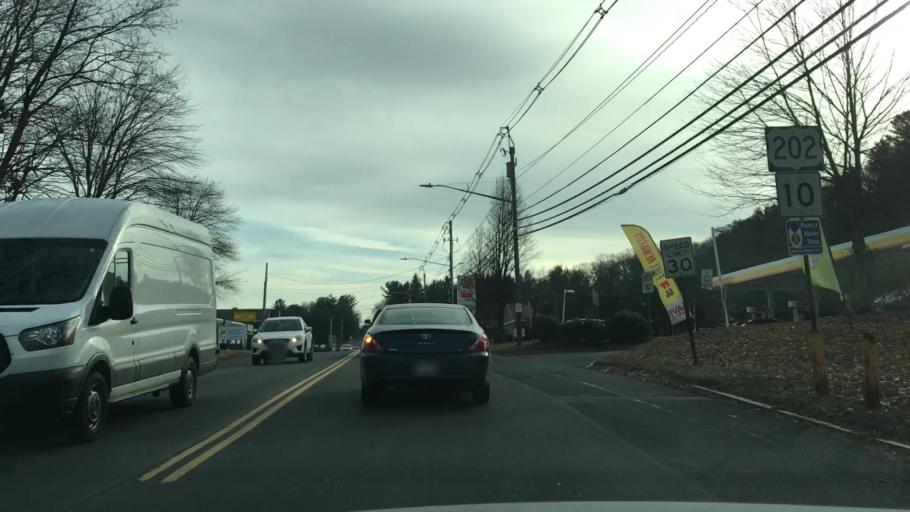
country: US
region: Massachusetts
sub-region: Hampden County
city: Westfield
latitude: 42.1104
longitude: -72.7647
